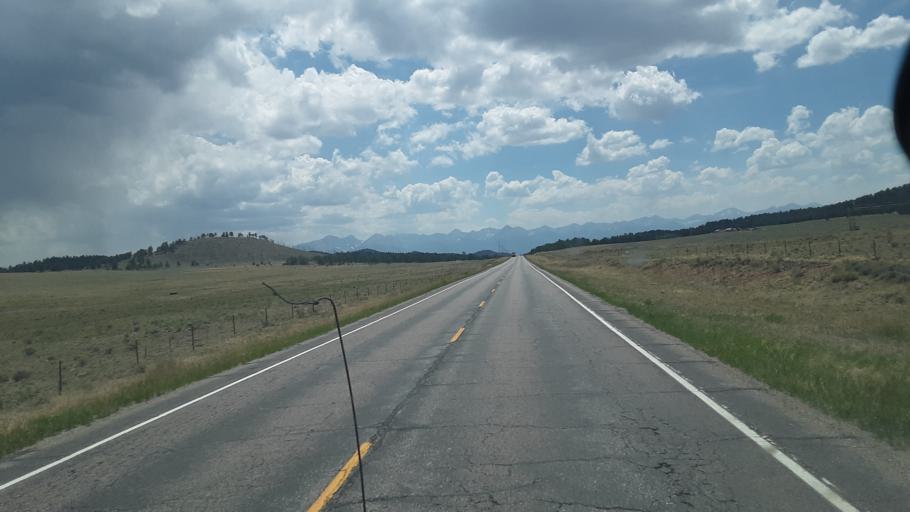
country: US
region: Colorado
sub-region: Custer County
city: Westcliffe
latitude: 38.1614
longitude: -105.2935
